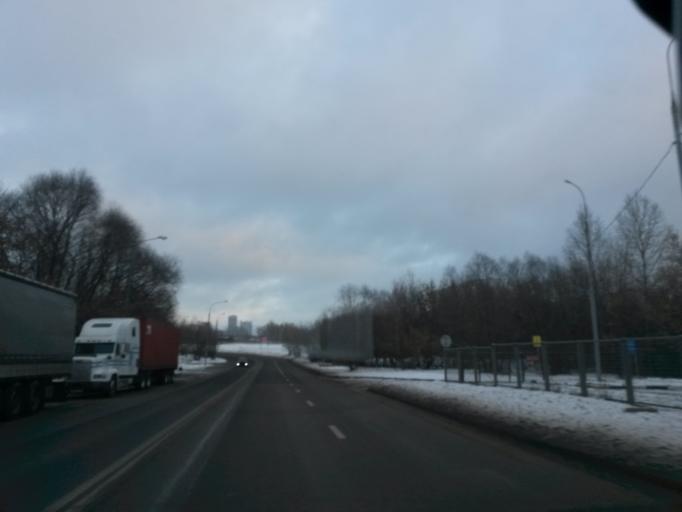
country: RU
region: Moscow
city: Amin'yevo
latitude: 55.7021
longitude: 37.4516
